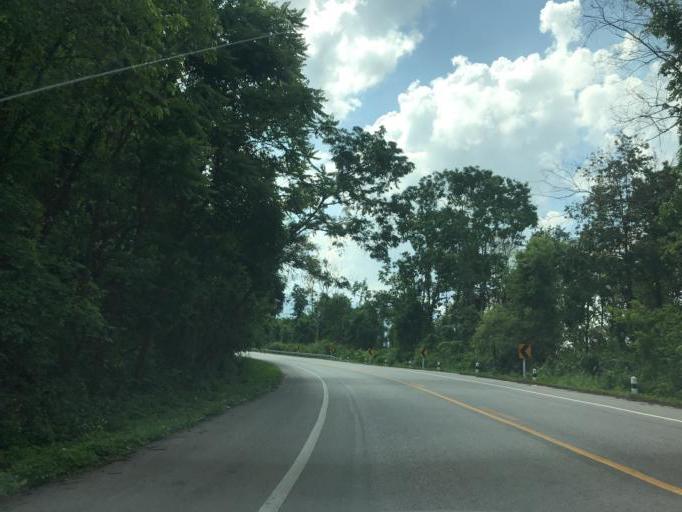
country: TH
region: Phayao
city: Phayao
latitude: 19.0888
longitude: 99.8133
